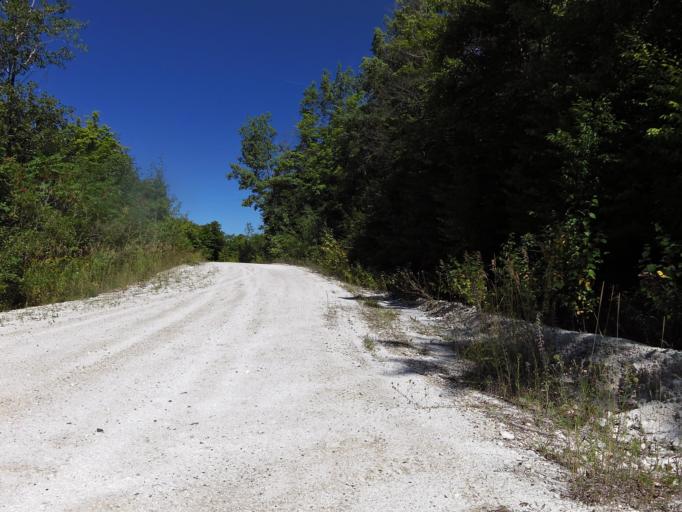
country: CA
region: Ontario
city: Arnprior
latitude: 45.1565
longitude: -76.4949
